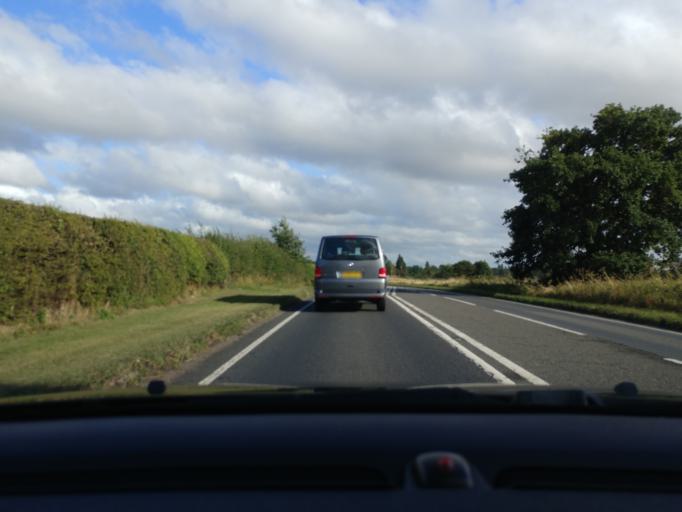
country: GB
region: England
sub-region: Oxfordshire
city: Radley
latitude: 51.6940
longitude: -1.2075
